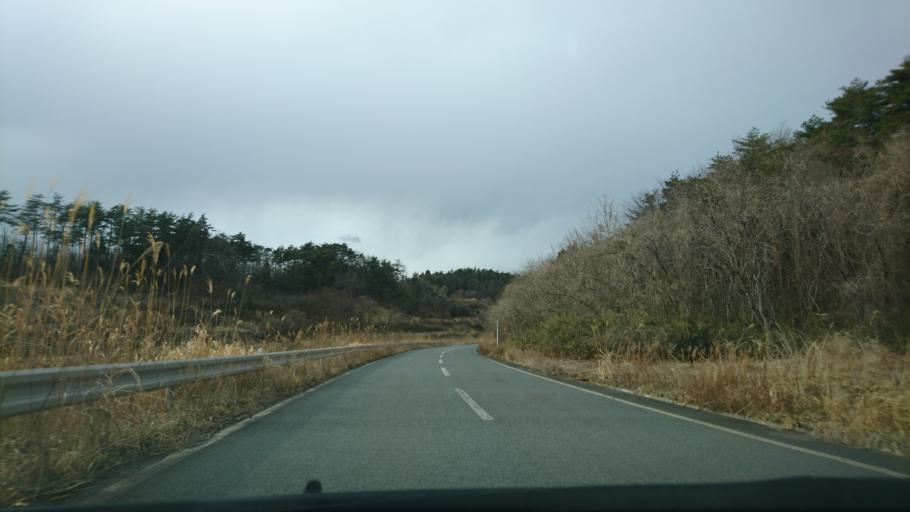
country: JP
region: Iwate
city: Ichinoseki
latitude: 38.8428
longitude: 141.2119
